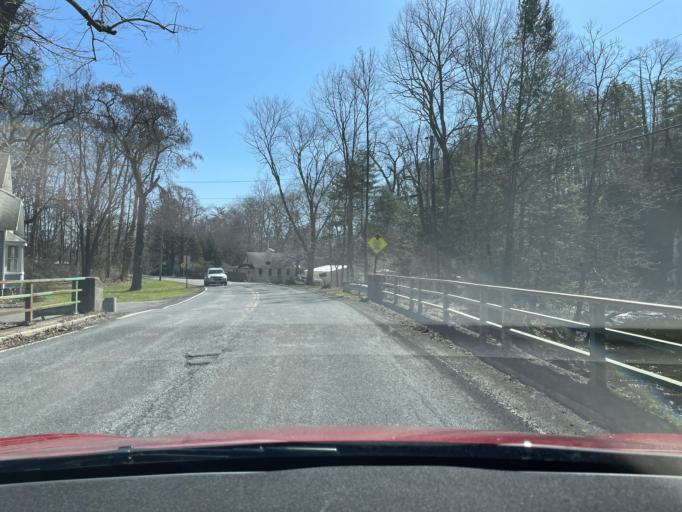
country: US
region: New York
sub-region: Ulster County
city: Glasco
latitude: 42.0406
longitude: -74.0027
